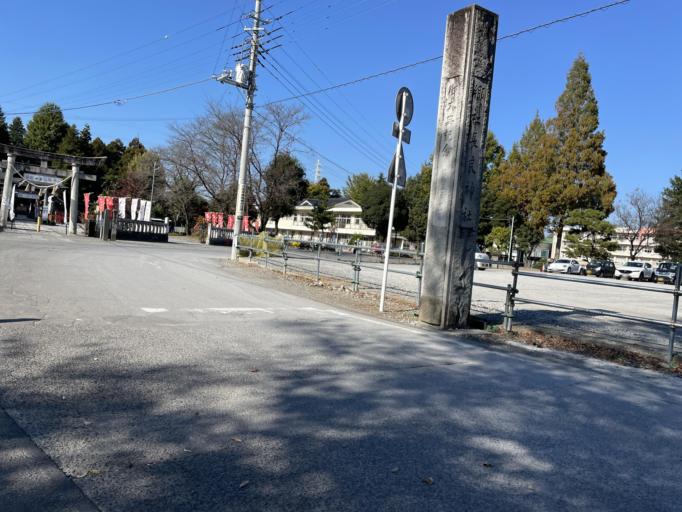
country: JP
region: Gunma
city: Tatebayashi
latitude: 36.2538
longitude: 139.5329
